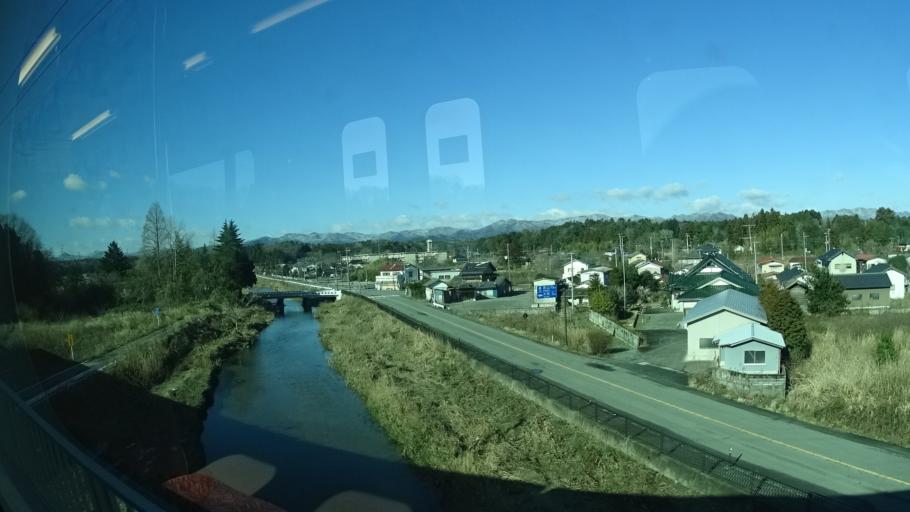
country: JP
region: Fukushima
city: Namie
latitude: 37.4403
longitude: 141.0016
